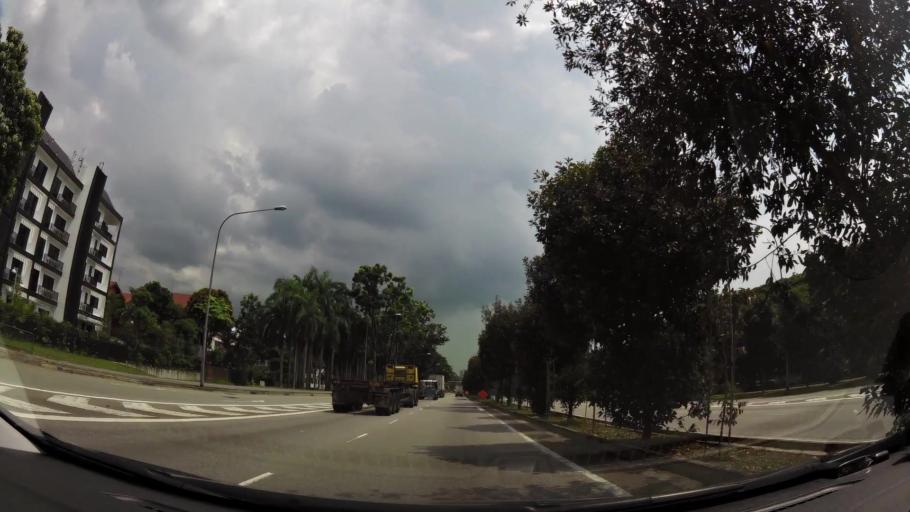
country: SG
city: Singapore
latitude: 1.2905
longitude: 103.7701
